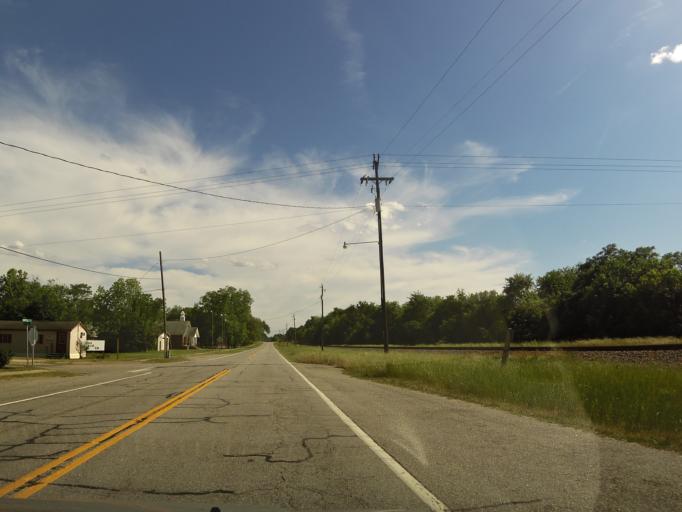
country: US
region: South Carolina
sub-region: Bamberg County
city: Denmark
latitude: 33.2233
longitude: -81.1751
